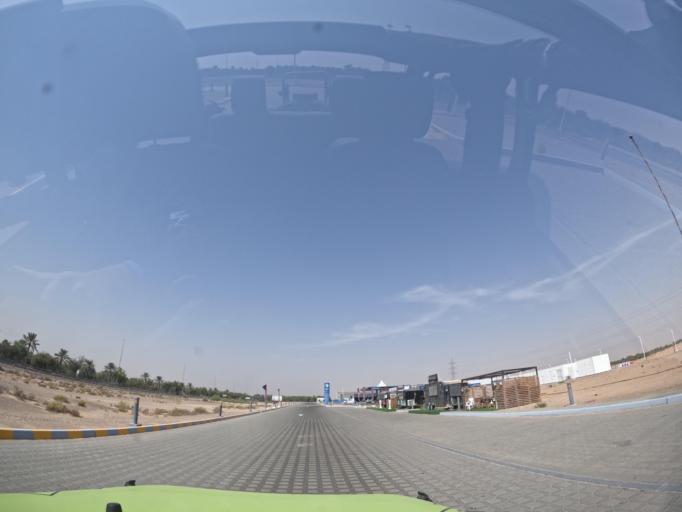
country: AE
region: Abu Dhabi
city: Al Ain
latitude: 24.1789
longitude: 55.1821
